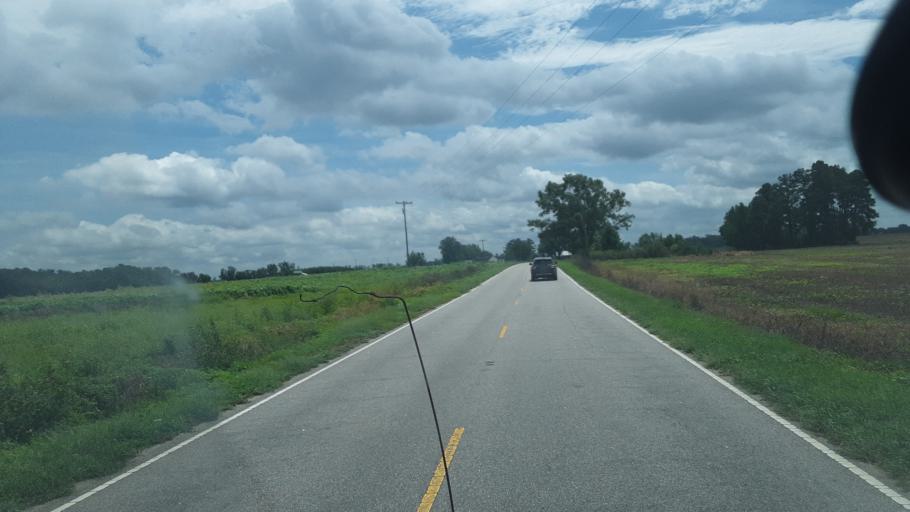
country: US
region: North Carolina
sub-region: Robeson County
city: Fairmont
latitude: 34.3839
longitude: -79.1172
